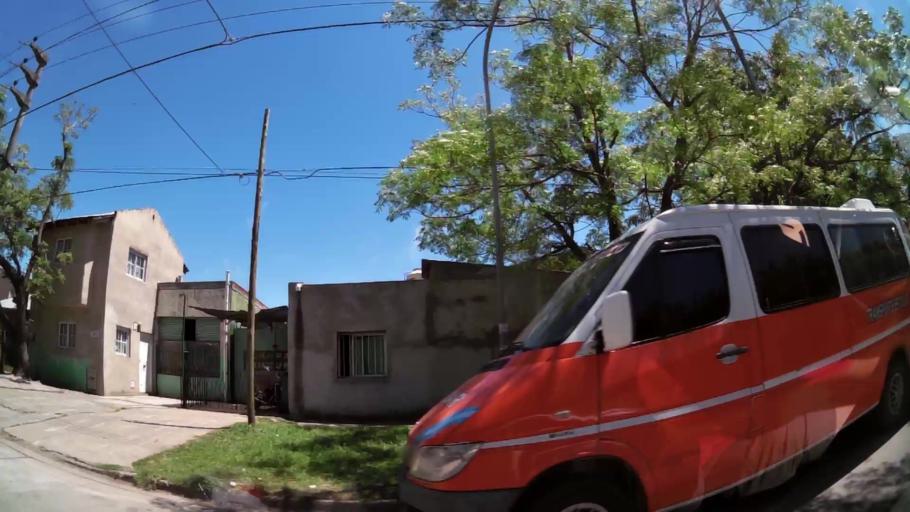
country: AR
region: Buenos Aires
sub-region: Partido de Tigre
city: Tigre
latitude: -34.4868
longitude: -58.6388
